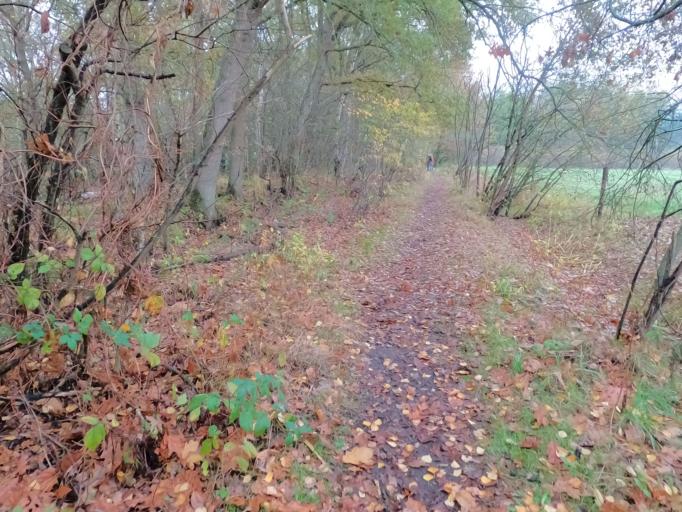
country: BE
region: Flanders
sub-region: Provincie Antwerpen
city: Nijlen
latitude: 51.1660
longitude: 4.6356
